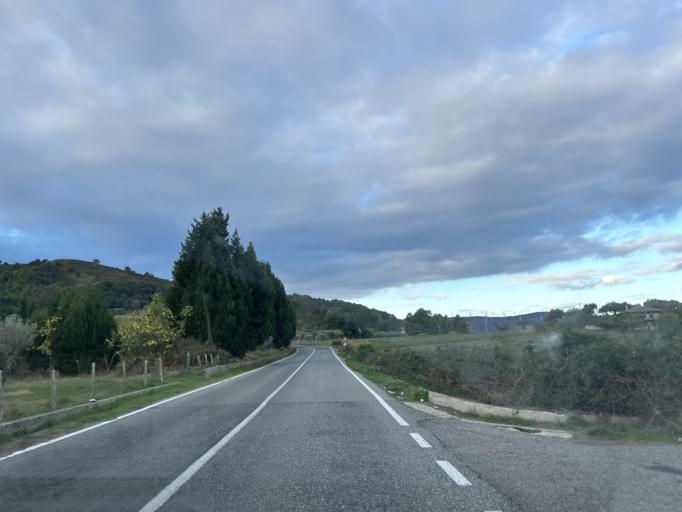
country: IT
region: Calabria
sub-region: Provincia di Catanzaro
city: Montauro
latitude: 38.7595
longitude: 16.5102
